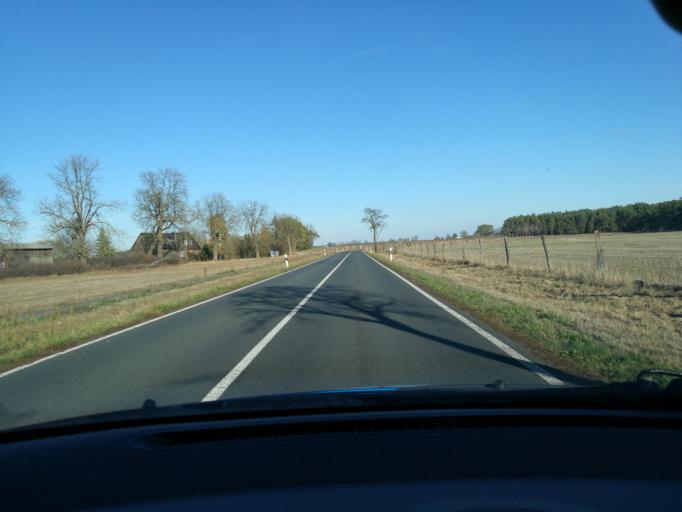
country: DE
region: Brandenburg
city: Lanz
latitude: 53.1561
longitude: 11.5925
